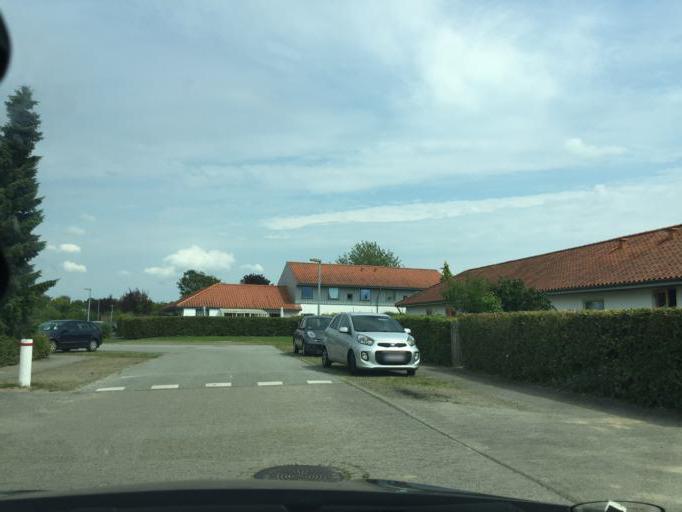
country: DK
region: South Denmark
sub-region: Odense Kommune
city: Neder Holluf
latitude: 55.3628
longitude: 10.4427
